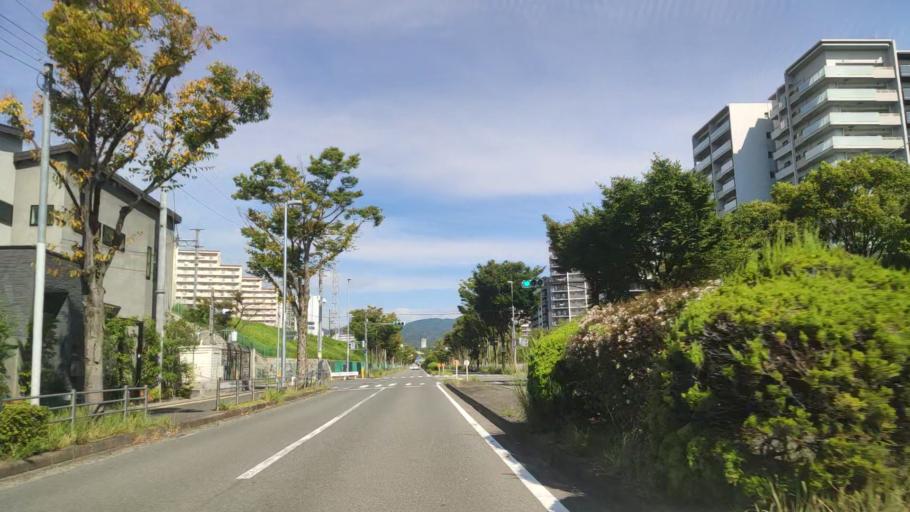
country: JP
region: Osaka
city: Mino
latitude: 34.8155
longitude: 135.5137
